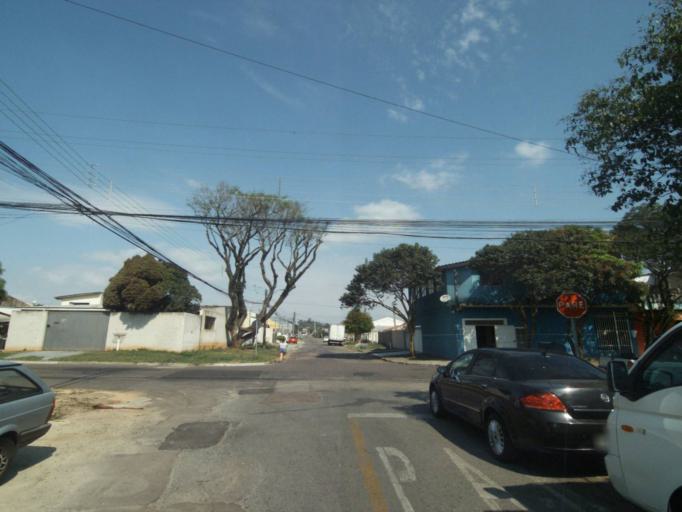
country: BR
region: Parana
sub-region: Curitiba
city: Curitiba
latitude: -25.4874
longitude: -49.3358
